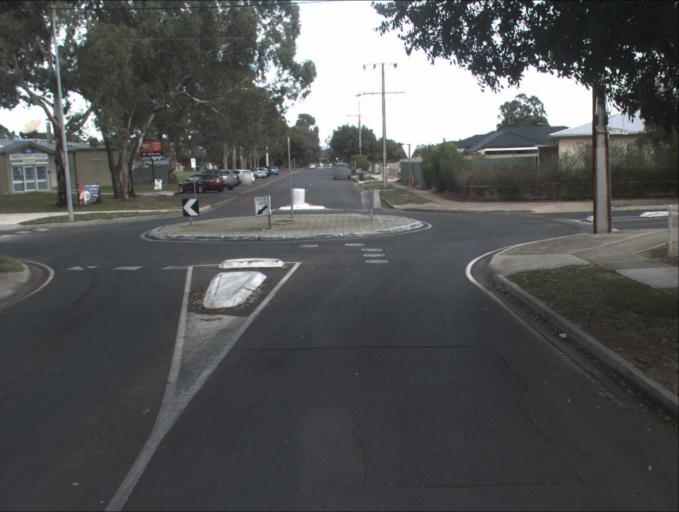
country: AU
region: South Australia
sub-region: Port Adelaide Enfield
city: Enfield
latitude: -34.8530
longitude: 138.6229
